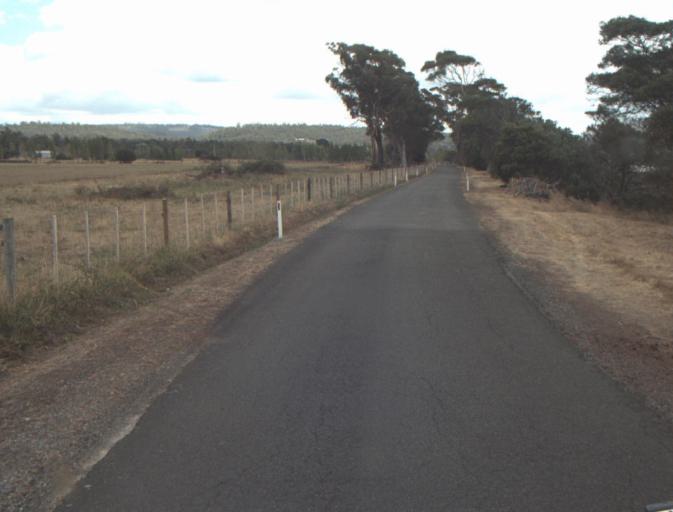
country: AU
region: Tasmania
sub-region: Launceston
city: Mayfield
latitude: -41.2866
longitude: 146.9980
